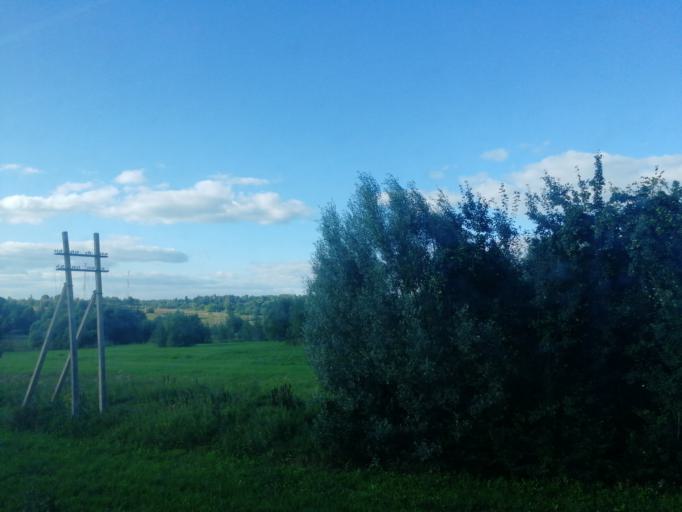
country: RU
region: Tula
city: Leninskiy
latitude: 54.2628
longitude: 37.2911
